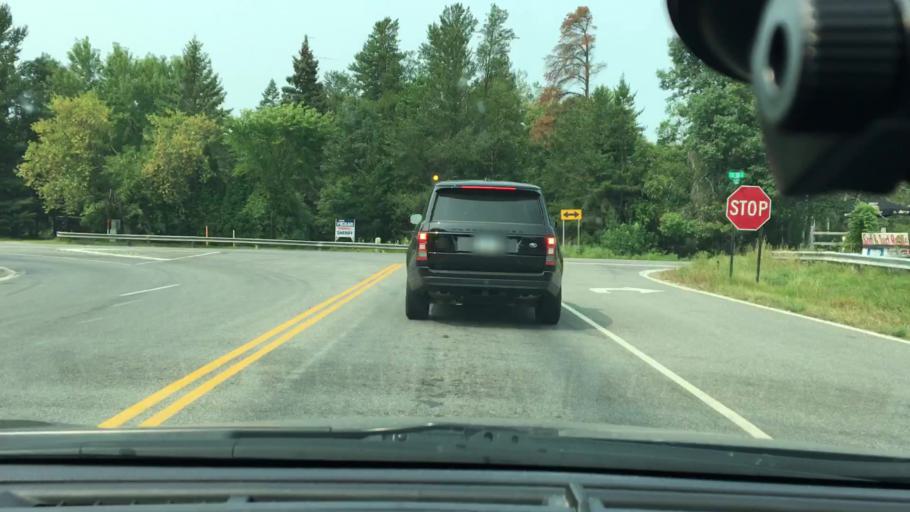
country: US
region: Minnesota
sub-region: Crow Wing County
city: Breezy Point
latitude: 46.4819
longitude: -94.1725
